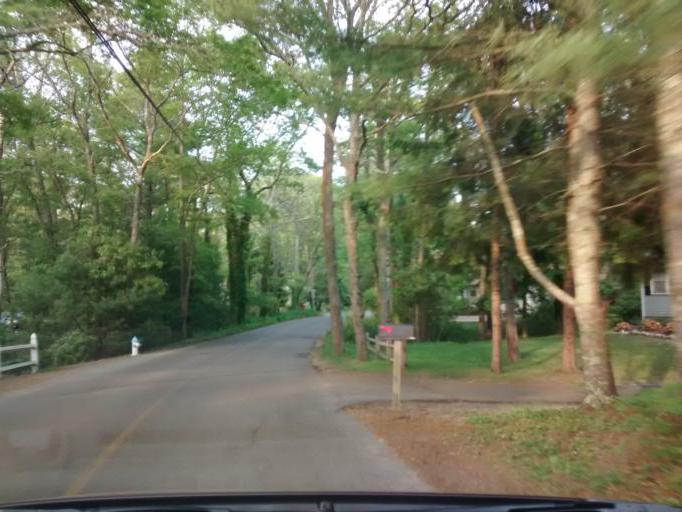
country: US
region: Massachusetts
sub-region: Barnstable County
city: Teaticket
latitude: 41.5915
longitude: -70.5865
